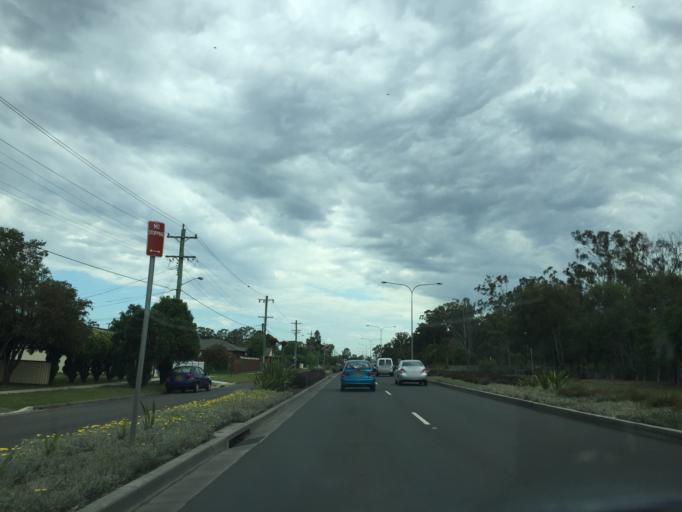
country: AU
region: New South Wales
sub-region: Blacktown
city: Doonside
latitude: -33.7562
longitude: 150.8646
